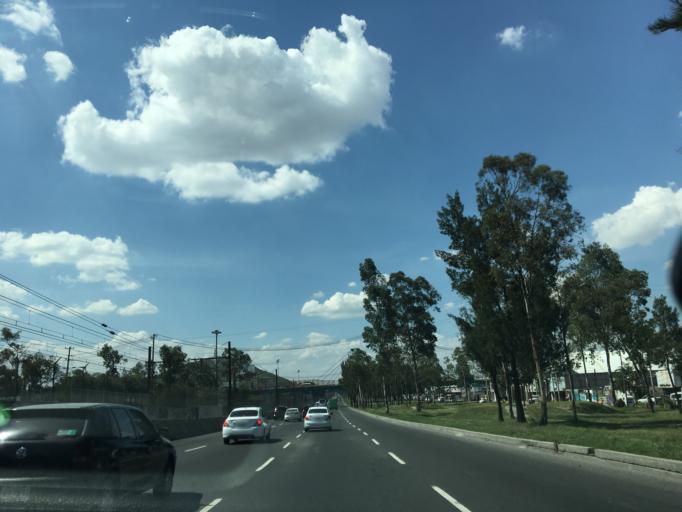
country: MX
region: Mexico
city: Ciudad Nezahualcoyotl
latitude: 19.3709
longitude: -99.0135
